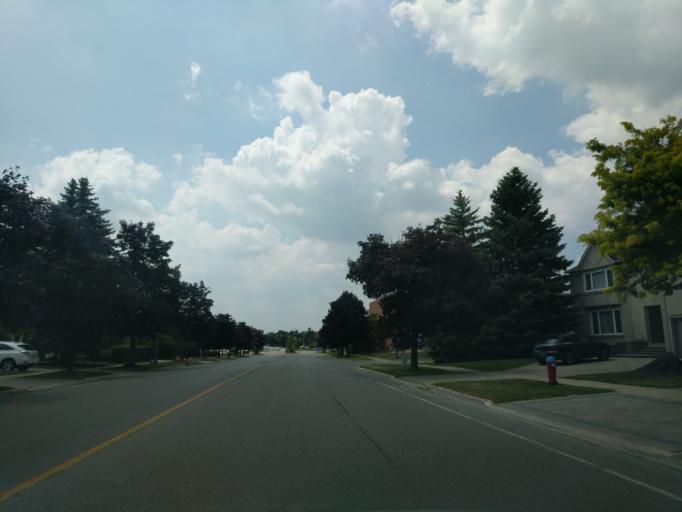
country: CA
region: Ontario
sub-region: York
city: Richmond Hill
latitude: 43.8693
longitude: -79.4110
